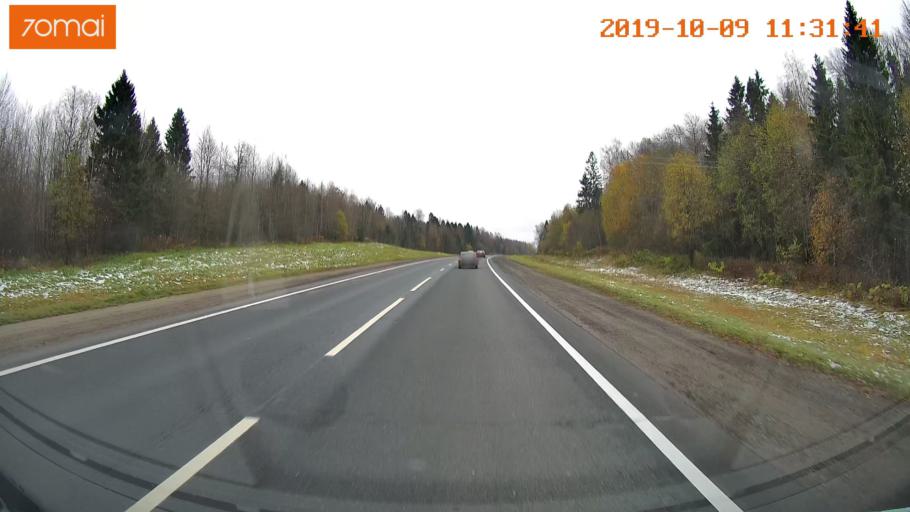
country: RU
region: Vologda
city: Gryazovets
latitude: 59.0432
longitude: 40.1006
